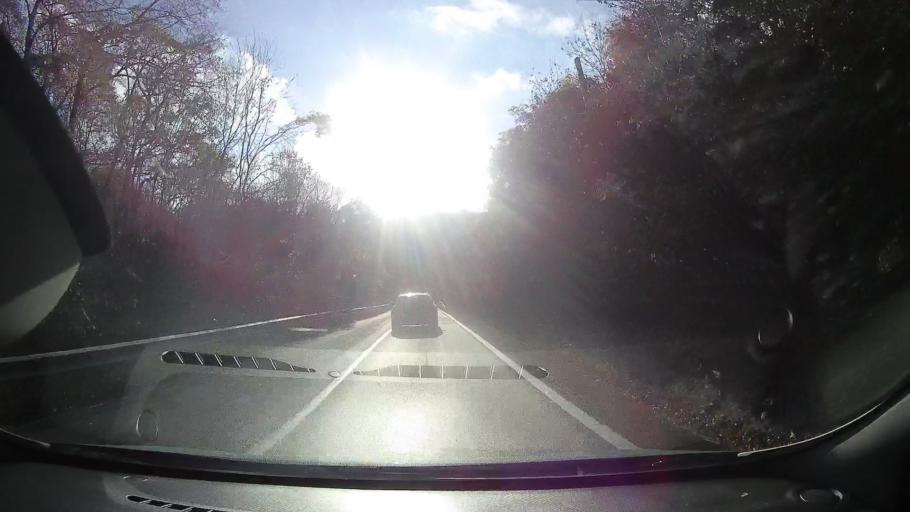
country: RO
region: Tulcea
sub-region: Comuna Topolog
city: Topolog
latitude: 44.9141
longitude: 28.4201
